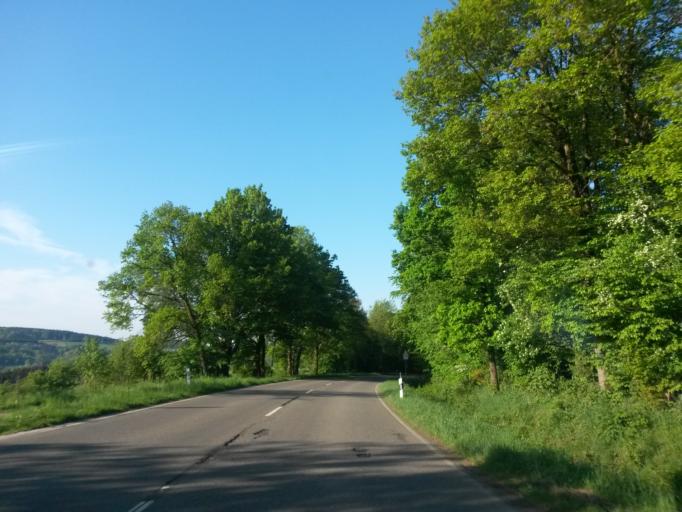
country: DE
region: North Rhine-Westphalia
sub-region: Regierungsbezirk Koln
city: Numbrecht
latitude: 50.9136
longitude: 7.4889
